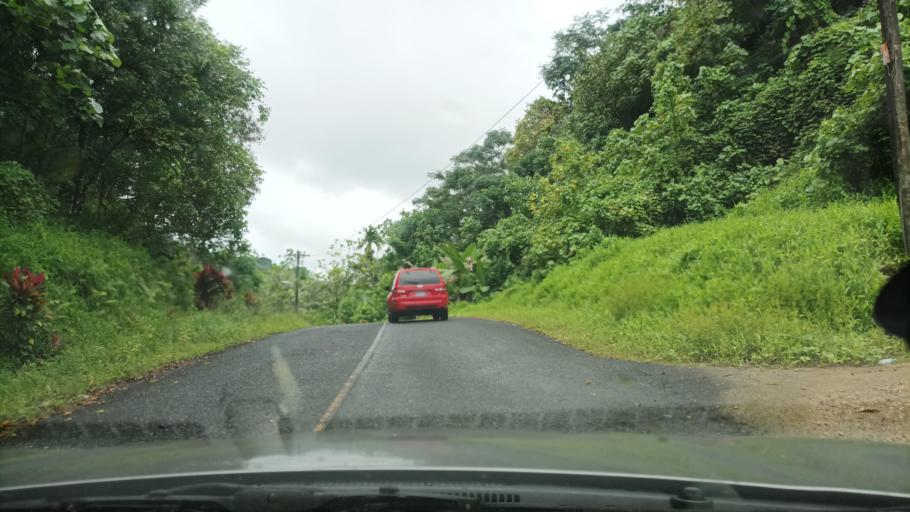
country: FM
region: Pohnpei
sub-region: Madolenihm Municipality
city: Madolenihm Municipality Government
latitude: 6.8043
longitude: 158.2681
